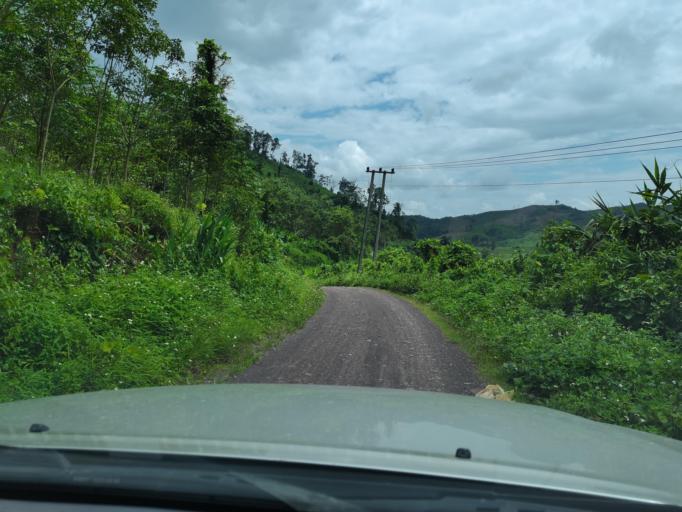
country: LA
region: Loungnamtha
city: Muang Long
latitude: 20.7143
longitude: 101.0138
